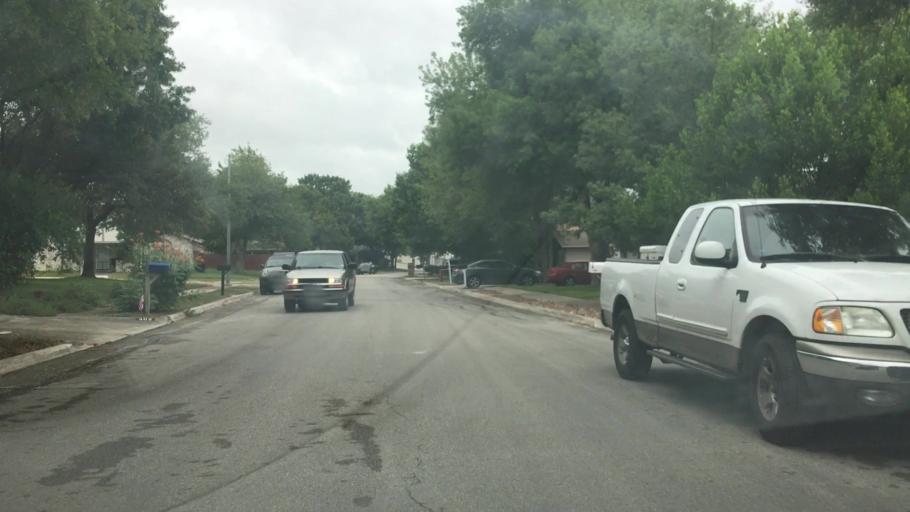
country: US
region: Texas
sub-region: Bexar County
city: Universal City
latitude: 29.5493
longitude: -98.3144
